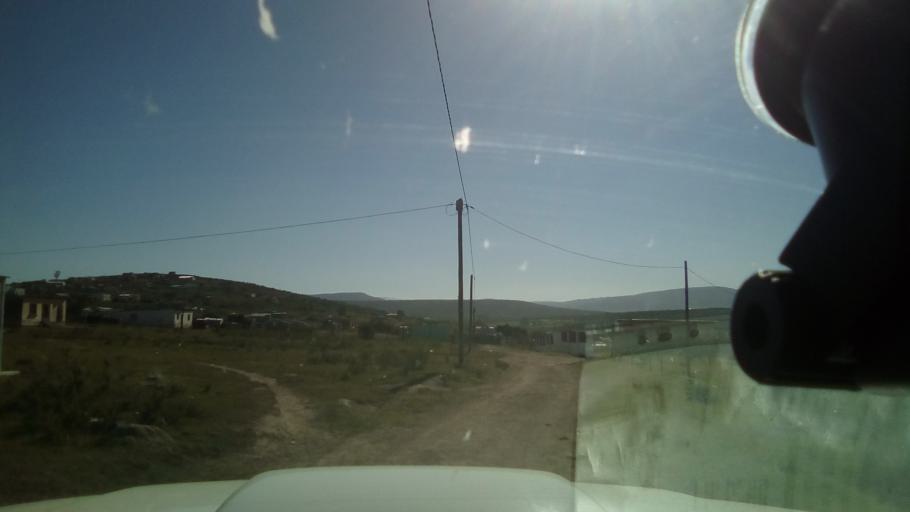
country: ZA
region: Eastern Cape
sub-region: Buffalo City Metropolitan Municipality
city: Bhisho
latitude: -32.8101
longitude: 27.3688
